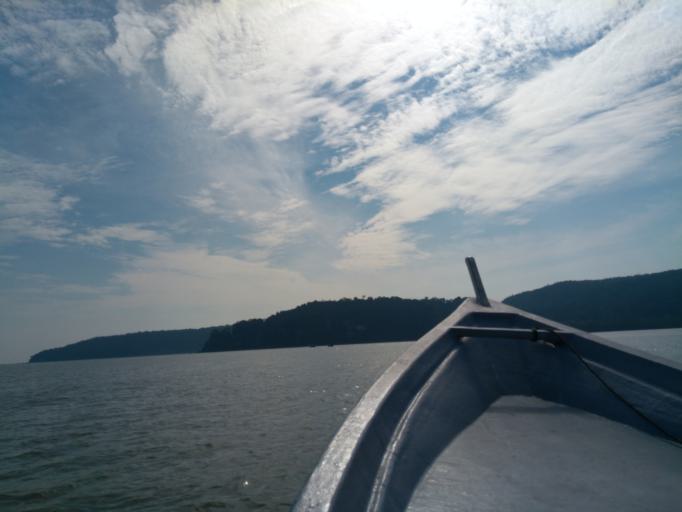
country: MY
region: Sarawak
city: Kuching
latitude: 1.7084
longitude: 110.4326
